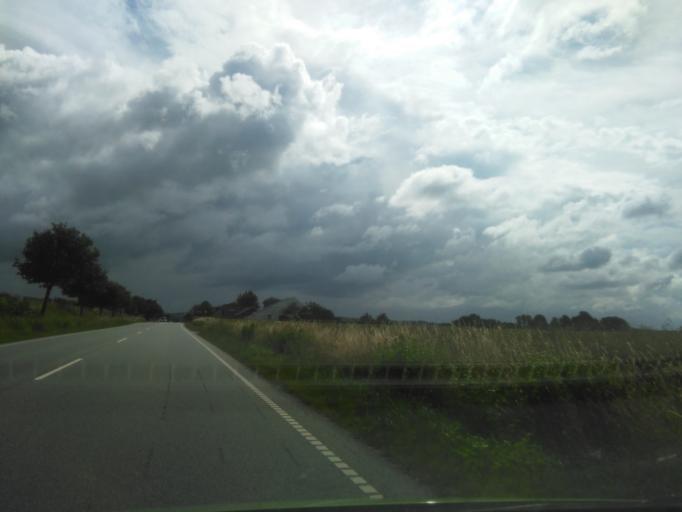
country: DK
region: Central Jutland
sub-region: Syddjurs Kommune
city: Ronde
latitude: 56.3054
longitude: 10.4341
